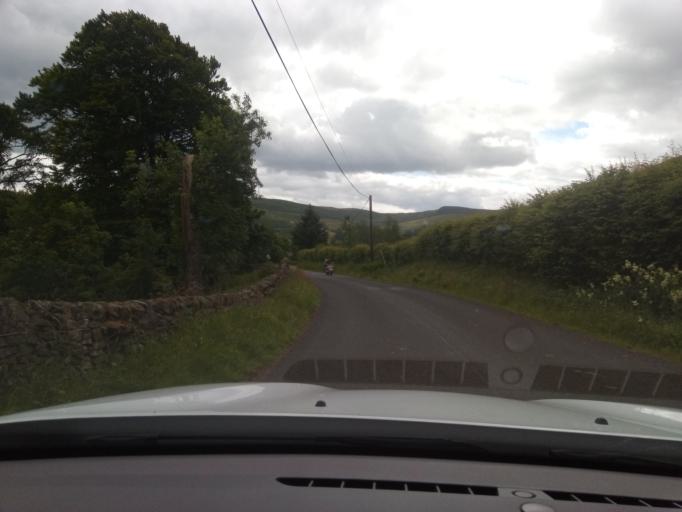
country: GB
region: Scotland
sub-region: The Scottish Borders
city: Innerleithen
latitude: 55.4501
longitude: -3.1033
